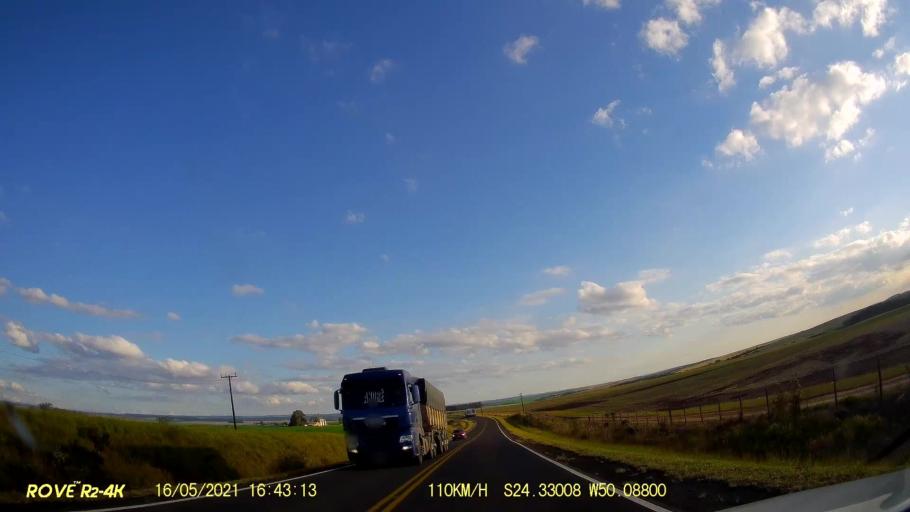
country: BR
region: Parana
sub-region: Pirai Do Sul
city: Pirai do Sul
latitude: -24.3307
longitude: -50.0881
